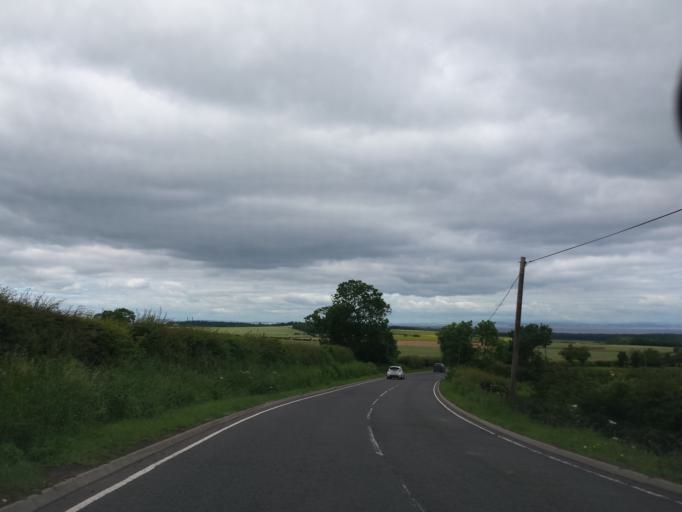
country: GB
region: Scotland
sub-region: East Lothian
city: Haddington
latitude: 55.9789
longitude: -2.8135
